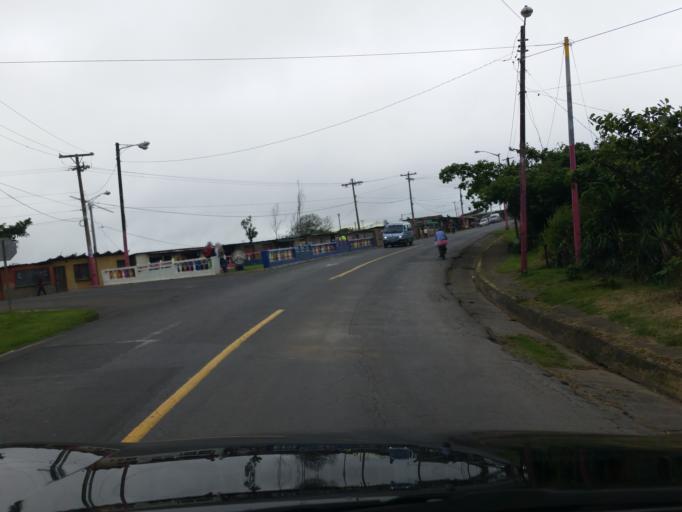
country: NI
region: Managua
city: El Crucero
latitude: 11.9925
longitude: -86.3092
